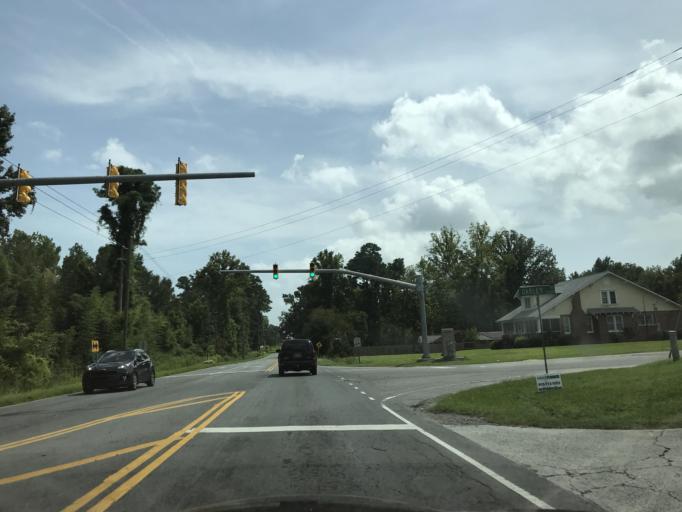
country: US
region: North Carolina
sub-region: New Hanover County
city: Wrightsboro
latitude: 34.3026
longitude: -77.9218
